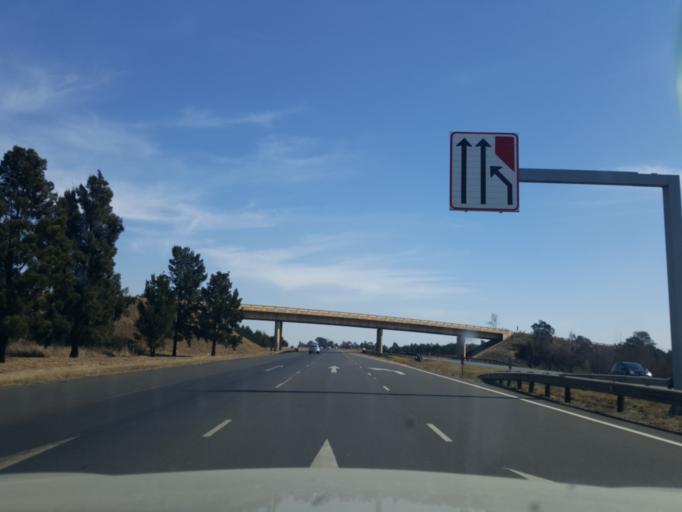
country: ZA
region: Mpumalanga
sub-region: Nkangala District Municipality
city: Middelburg
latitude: -25.8333
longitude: 29.4364
